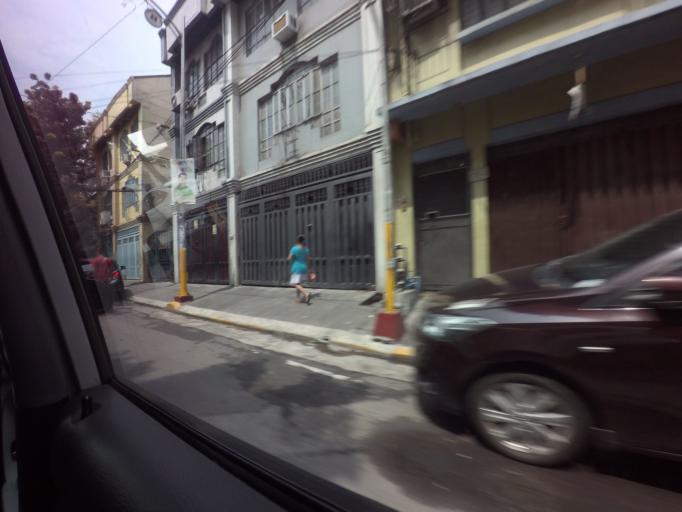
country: PH
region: Metro Manila
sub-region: City of Manila
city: Port Area
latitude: 14.5710
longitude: 120.9950
